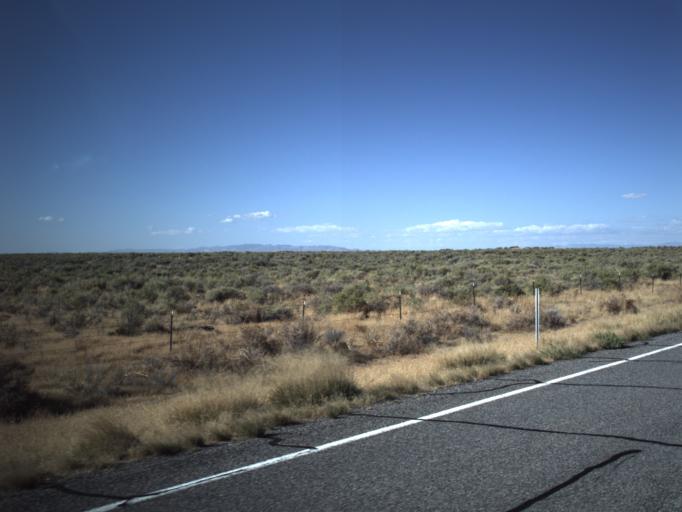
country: US
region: Utah
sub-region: Millard County
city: Delta
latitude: 39.3539
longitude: -112.4449
